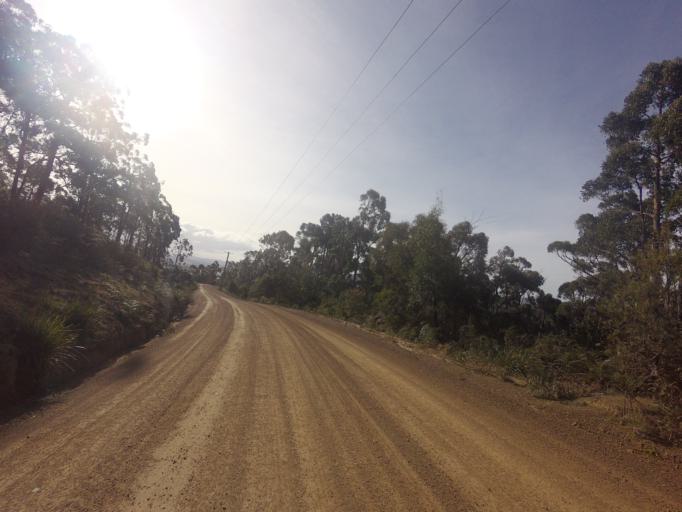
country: AU
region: Tasmania
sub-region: Kingborough
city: Kettering
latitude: -43.0839
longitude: 147.2646
